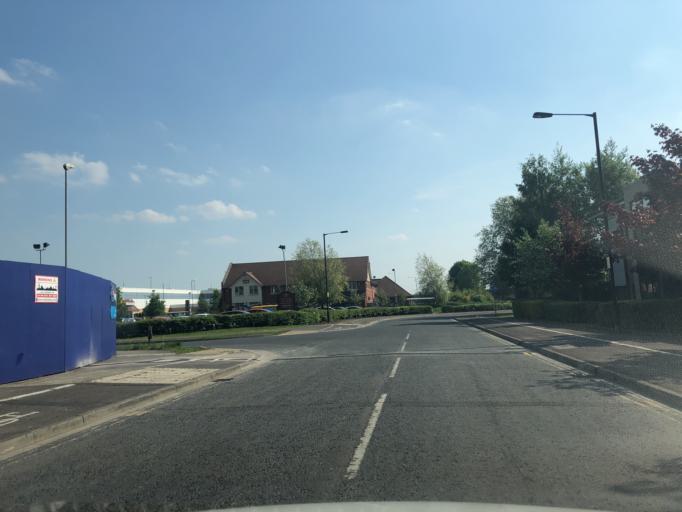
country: GB
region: England
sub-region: City of York
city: Huntington
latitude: 53.9906
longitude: -1.0477
